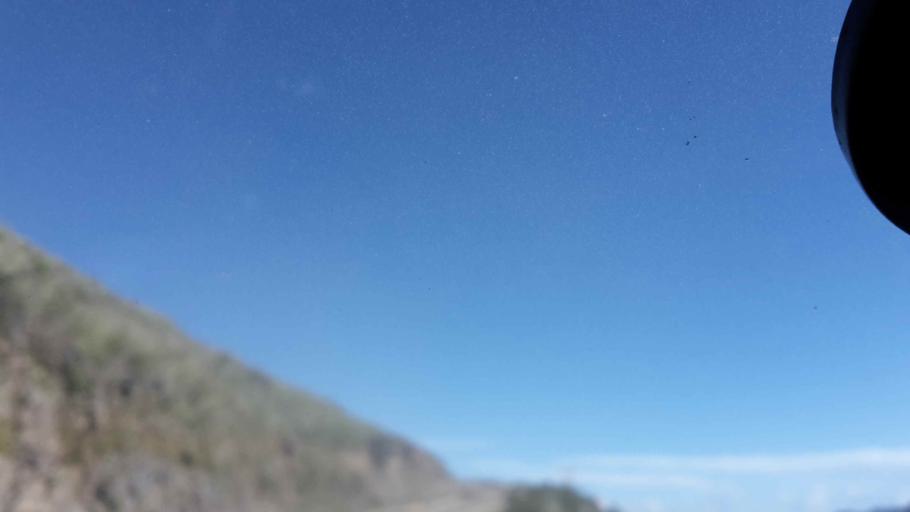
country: BO
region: Cochabamba
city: Arani
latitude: -17.7239
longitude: -65.6399
